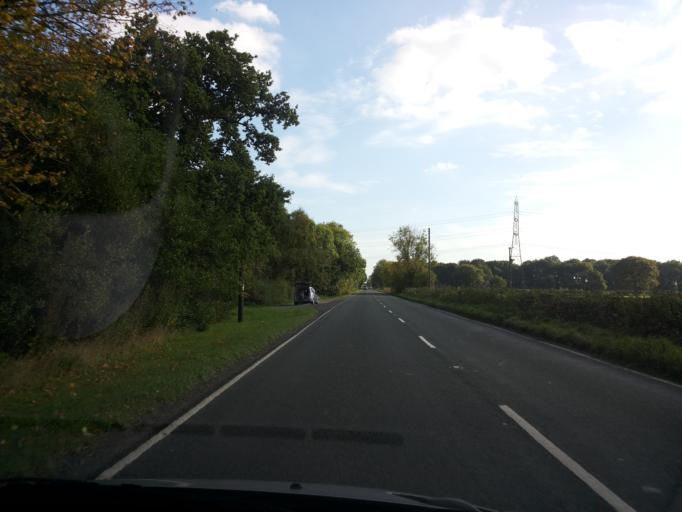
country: GB
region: England
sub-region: North Yorkshire
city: Camblesforth
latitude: 53.7415
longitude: -1.0454
